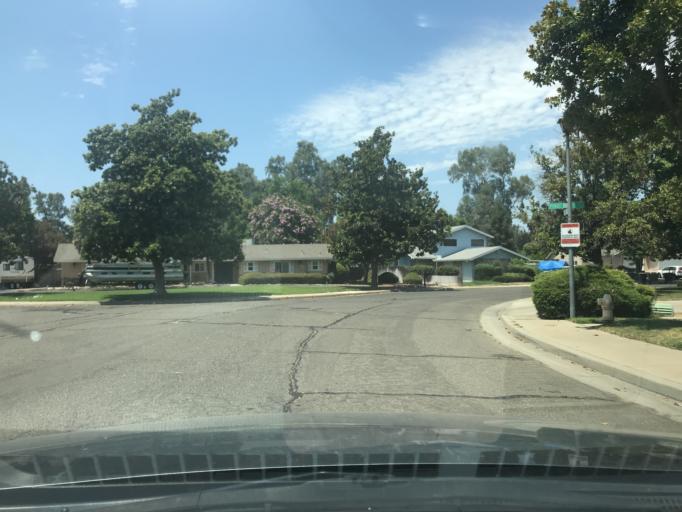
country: US
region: California
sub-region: Merced County
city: Atwater
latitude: 37.3652
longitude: -120.6077
